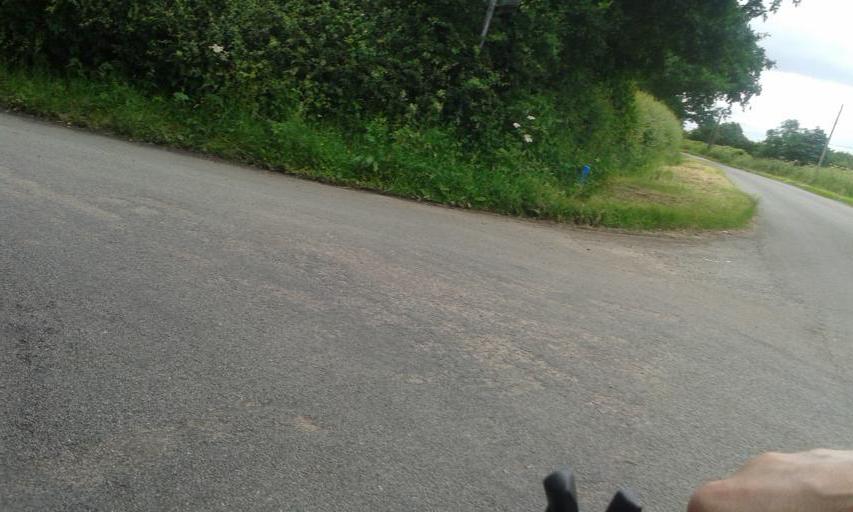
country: GB
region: England
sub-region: Leicestershire
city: Earl Shilton
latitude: 52.5787
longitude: -1.2911
